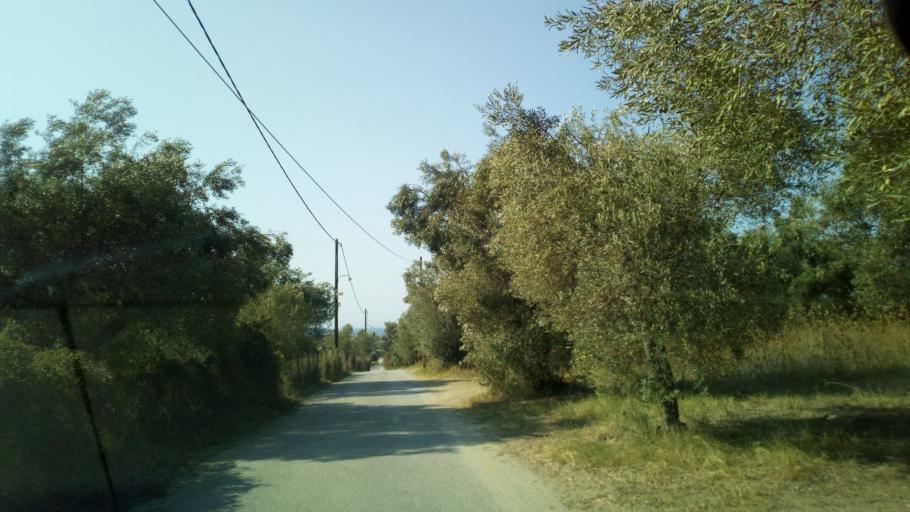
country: GR
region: Central Macedonia
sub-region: Nomos Chalkidikis
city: Pefkochori
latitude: 39.9736
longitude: 23.6531
